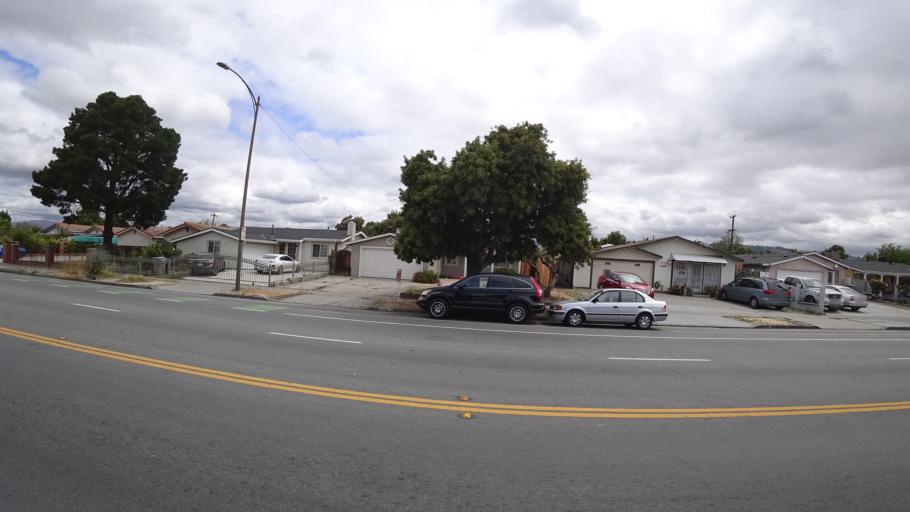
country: US
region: California
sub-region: Santa Clara County
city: Alum Rock
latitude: 37.3277
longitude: -121.8313
